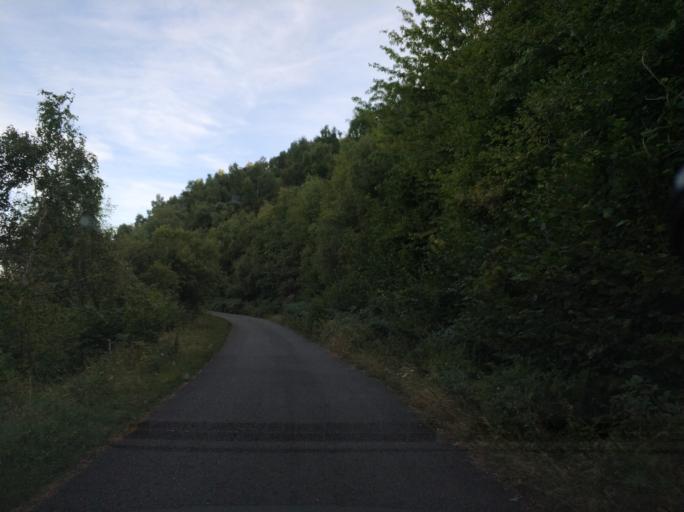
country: IT
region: Piedmont
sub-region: Provincia di Torino
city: Monastero di Lanzo
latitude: 45.3216
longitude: 7.4195
